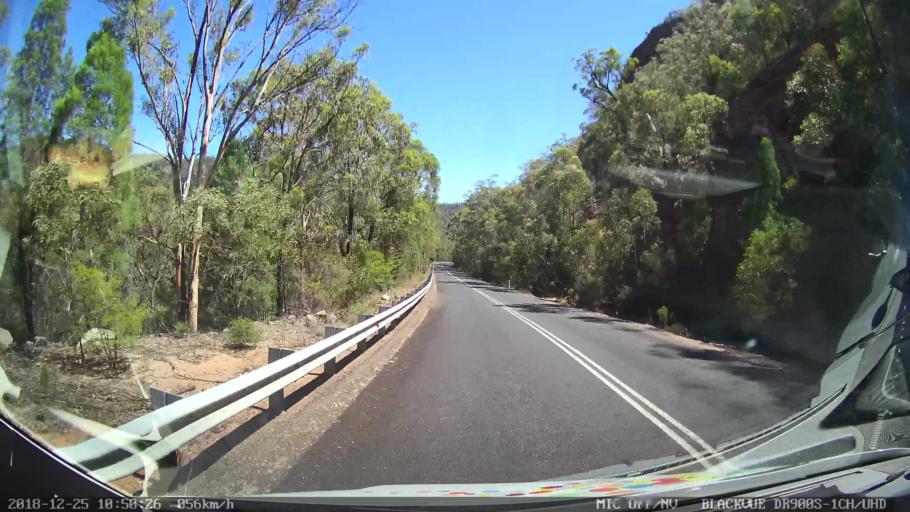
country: AU
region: New South Wales
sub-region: Upper Hunter Shire
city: Merriwa
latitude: -32.4461
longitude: 150.2681
